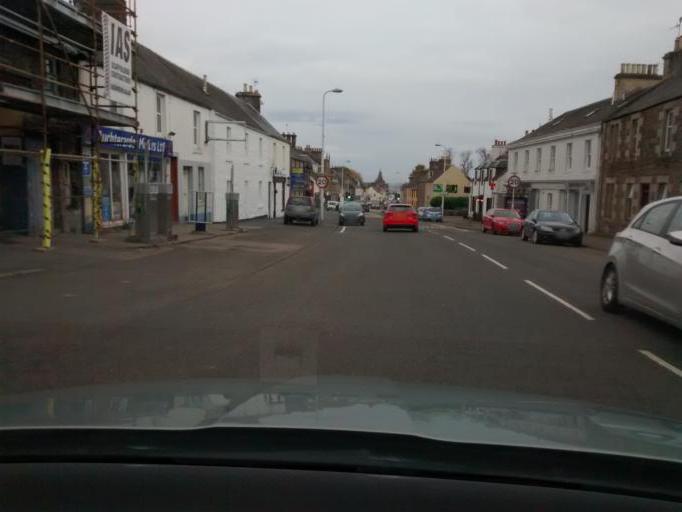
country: GB
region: Scotland
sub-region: Perth and Kinross
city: Auchterarder
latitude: 56.2945
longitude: -3.7119
